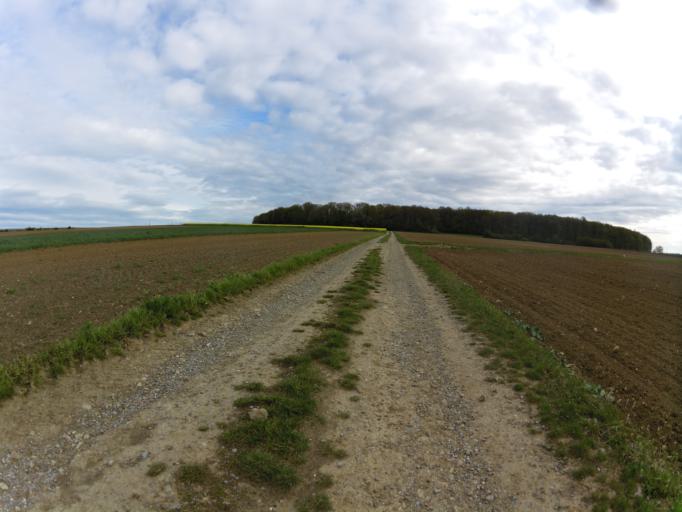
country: DE
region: Bavaria
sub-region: Regierungsbezirk Unterfranken
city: Prosselsheim
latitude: 49.8643
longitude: 10.1512
